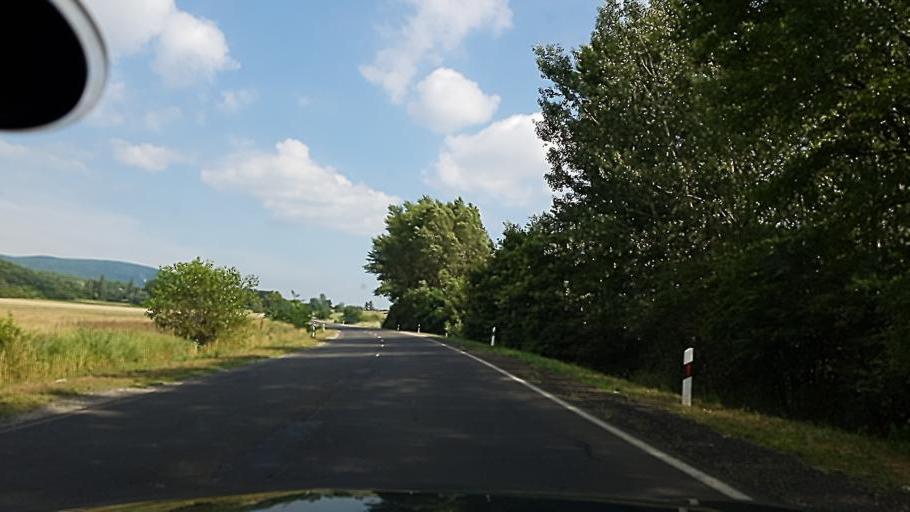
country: HU
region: Komarom-Esztergom
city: Dorog
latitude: 47.7243
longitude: 18.7657
